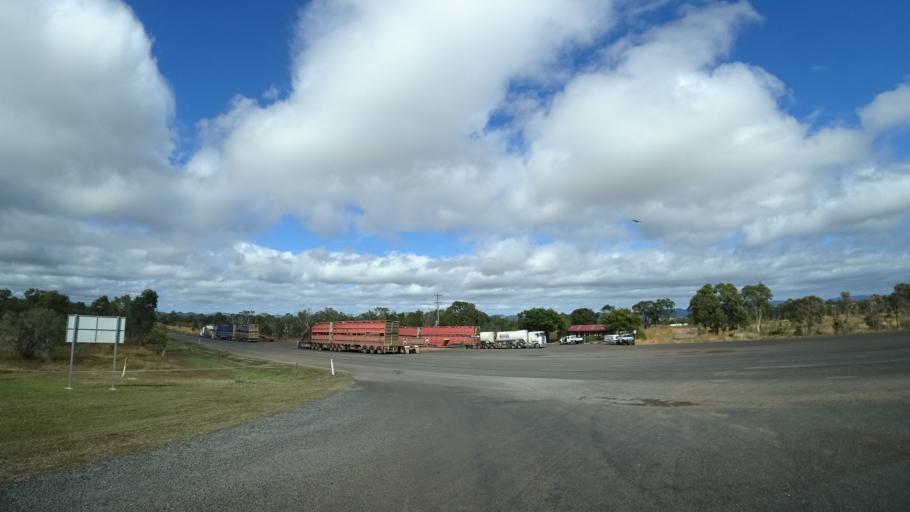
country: AU
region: Queensland
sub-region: Cook
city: Cooktown
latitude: -15.8633
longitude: 144.8585
